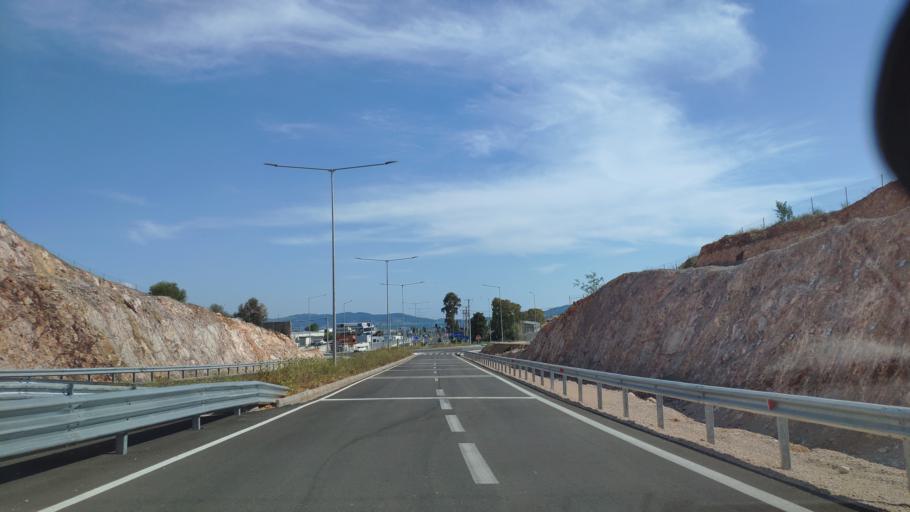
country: GR
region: Attica
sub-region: Nomarchia Dytikis Attikis
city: Mandra
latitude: 38.0786
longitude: 23.5069
